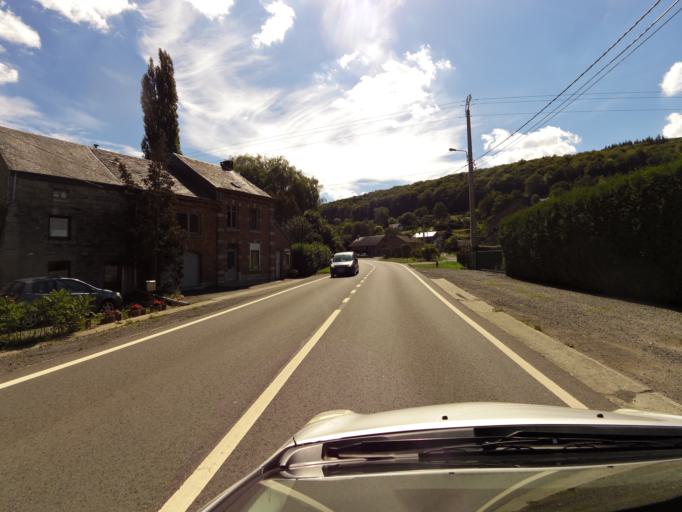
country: BE
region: Wallonia
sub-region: Province du Luxembourg
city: Hotton
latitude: 50.2565
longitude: 5.4760
